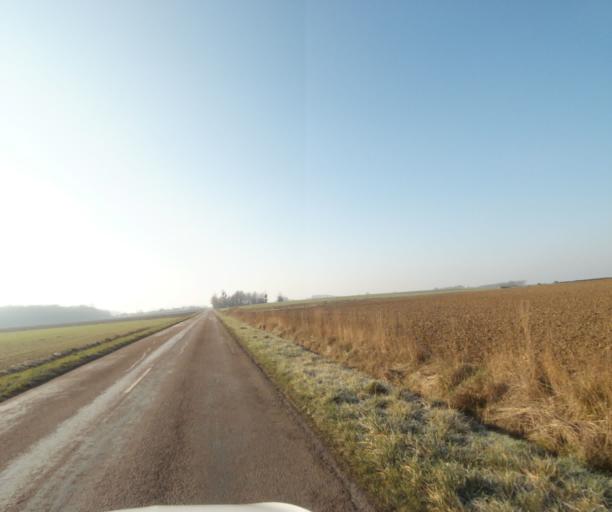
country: FR
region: Champagne-Ardenne
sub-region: Departement de la Haute-Marne
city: Montier-en-Der
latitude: 48.4480
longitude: 4.7631
